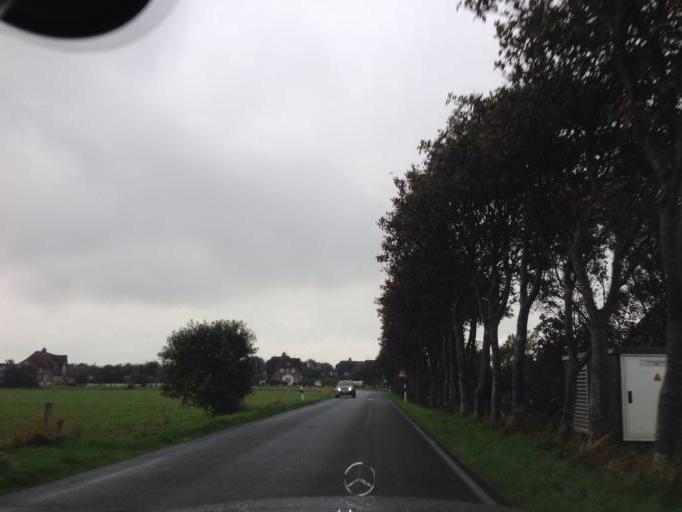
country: DE
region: Schleswig-Holstein
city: Dunsum
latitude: 54.7315
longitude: 8.4169
